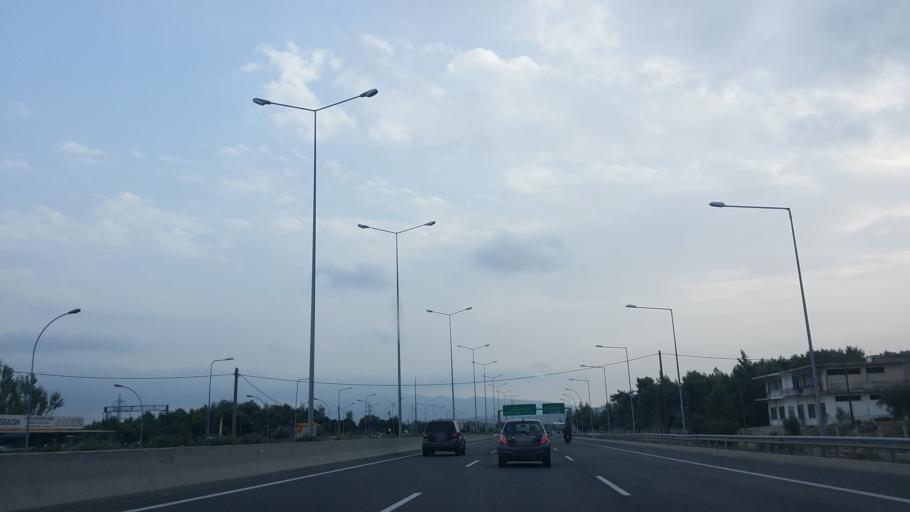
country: GR
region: Attica
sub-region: Nomarchia Anatolikis Attikis
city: Polydendri
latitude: 38.2088
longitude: 23.8551
